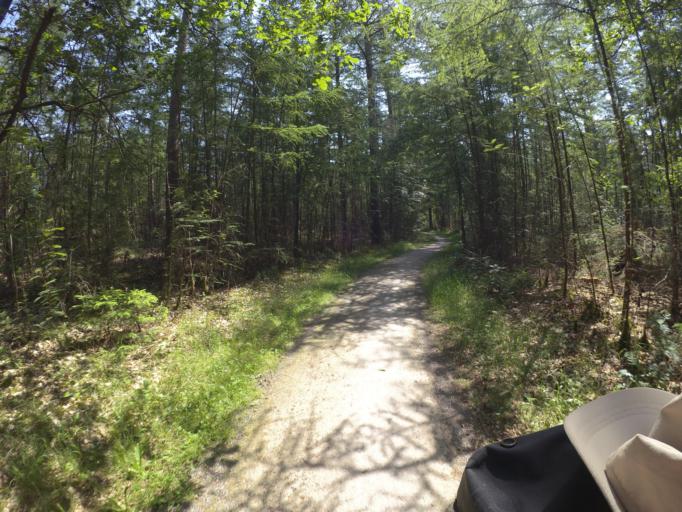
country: NL
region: Drenthe
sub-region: Gemeente De Wolden
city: Ruinen
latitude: 52.7293
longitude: 6.3742
